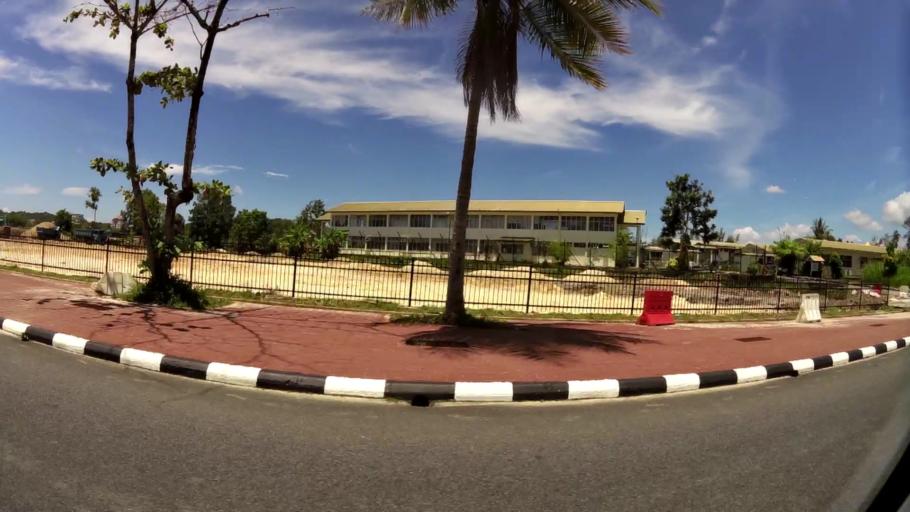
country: BN
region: Brunei and Muara
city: Bandar Seri Begawan
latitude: 4.9274
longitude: 114.9416
